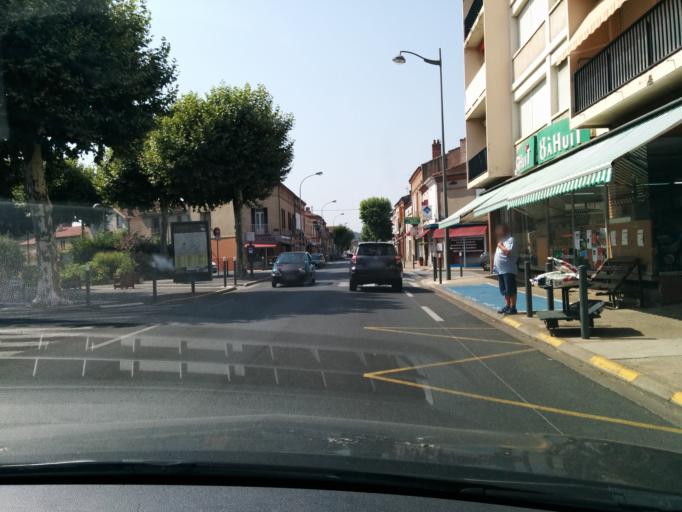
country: FR
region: Midi-Pyrenees
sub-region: Departement du Tarn
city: Albi
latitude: 43.9381
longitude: 2.1430
